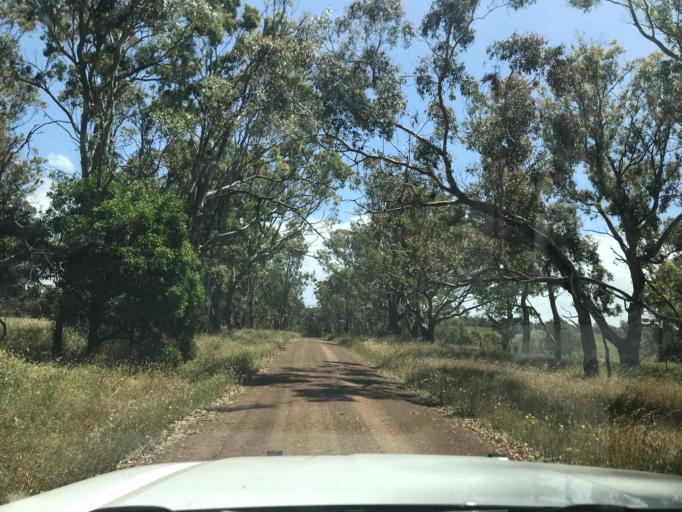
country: AU
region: South Australia
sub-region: Wattle Range
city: Penola
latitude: -37.2869
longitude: 141.4879
